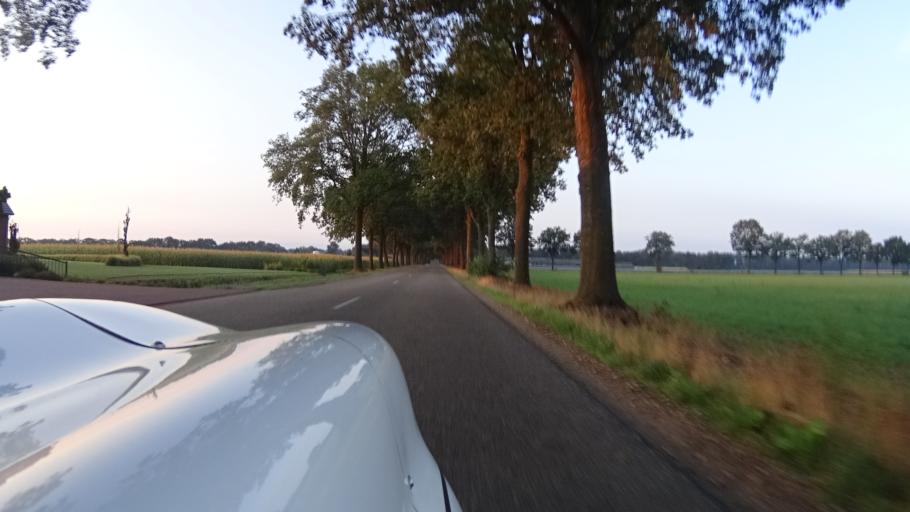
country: NL
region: North Brabant
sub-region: Gemeente Mill en Sint Hubert
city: Wilbertoord
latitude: 51.6093
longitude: 5.7828
